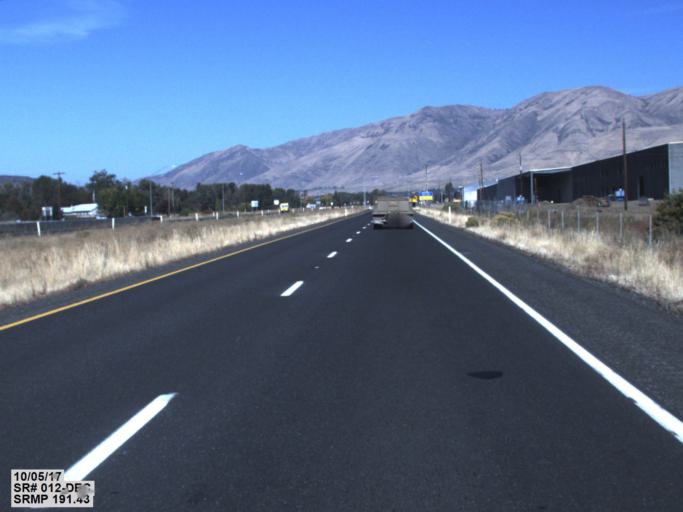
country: US
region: Washington
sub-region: Yakima County
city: Tieton
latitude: 46.7152
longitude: -120.6737
